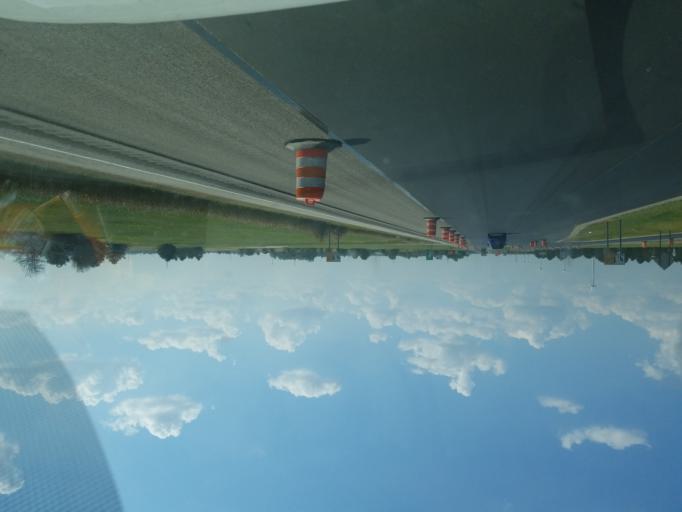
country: US
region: Ohio
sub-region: Van Wert County
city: Convoy
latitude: 40.9412
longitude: -84.7089
